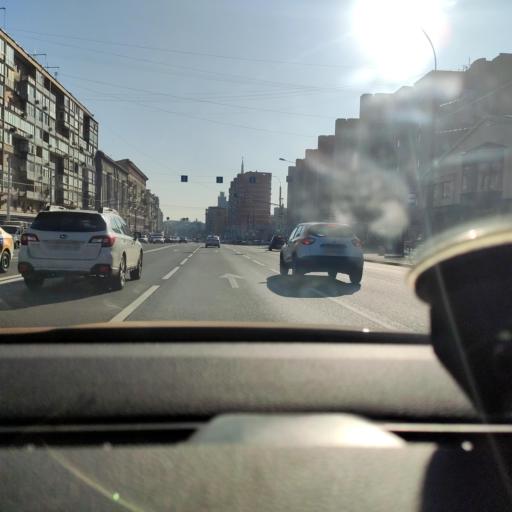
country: RU
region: Moskovskaya
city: Dorogomilovo
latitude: 55.7631
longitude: 37.5654
